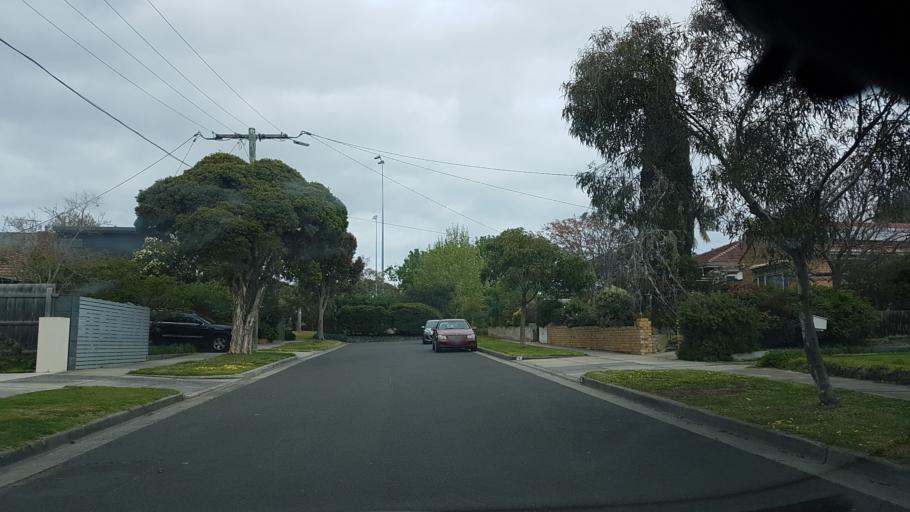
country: AU
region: Victoria
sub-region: Glen Eira
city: Bentleigh
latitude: -37.9226
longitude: 145.0303
